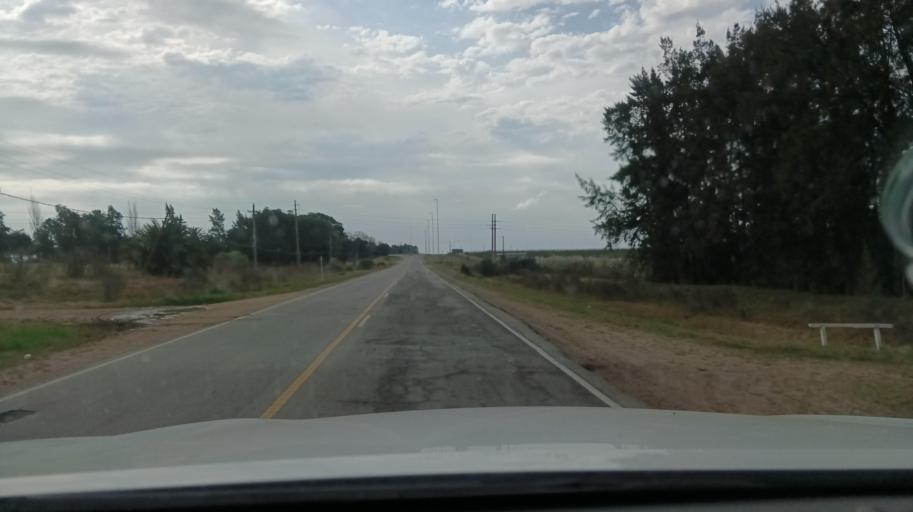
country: UY
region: Canelones
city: Sauce
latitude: -34.6710
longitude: -56.1147
